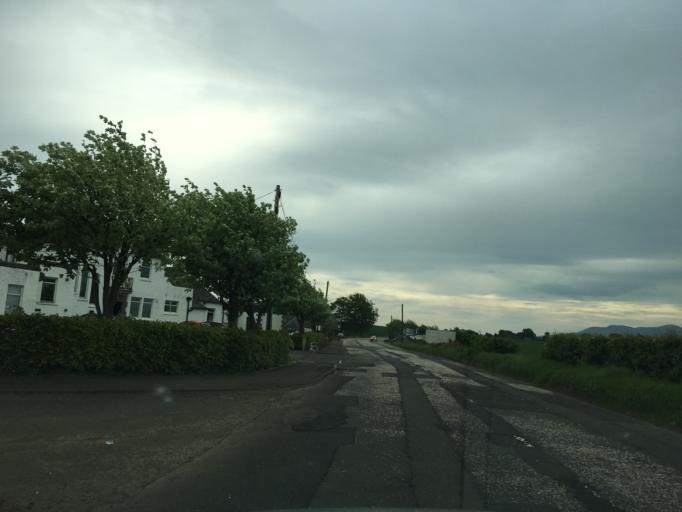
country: GB
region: Scotland
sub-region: Edinburgh
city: Ratho
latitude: 55.9502
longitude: -3.3366
